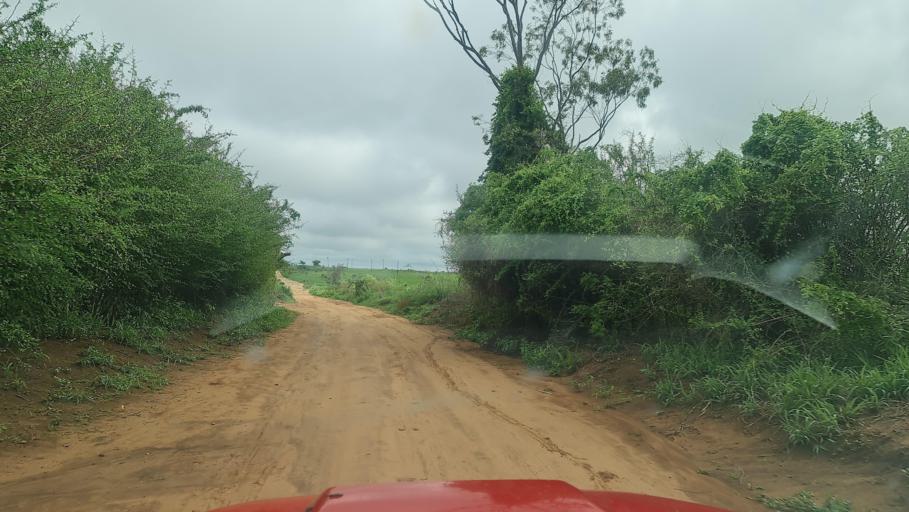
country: MW
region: Southern Region
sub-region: Nsanje District
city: Nsanje
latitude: -17.2020
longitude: 35.6989
